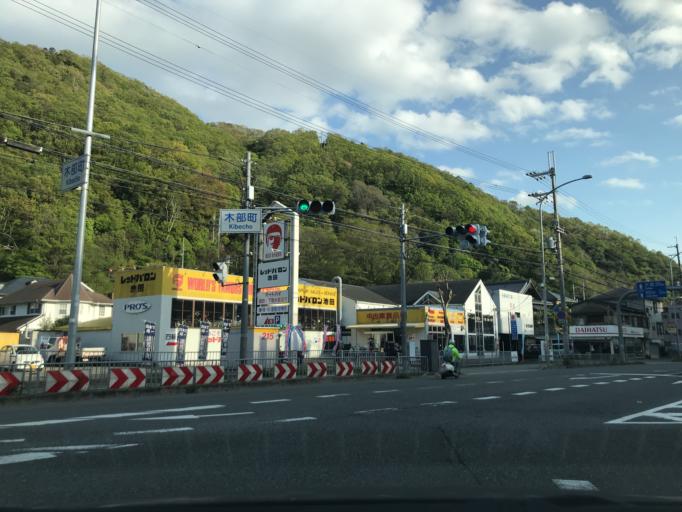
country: JP
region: Osaka
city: Ikeda
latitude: 34.8375
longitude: 135.4263
